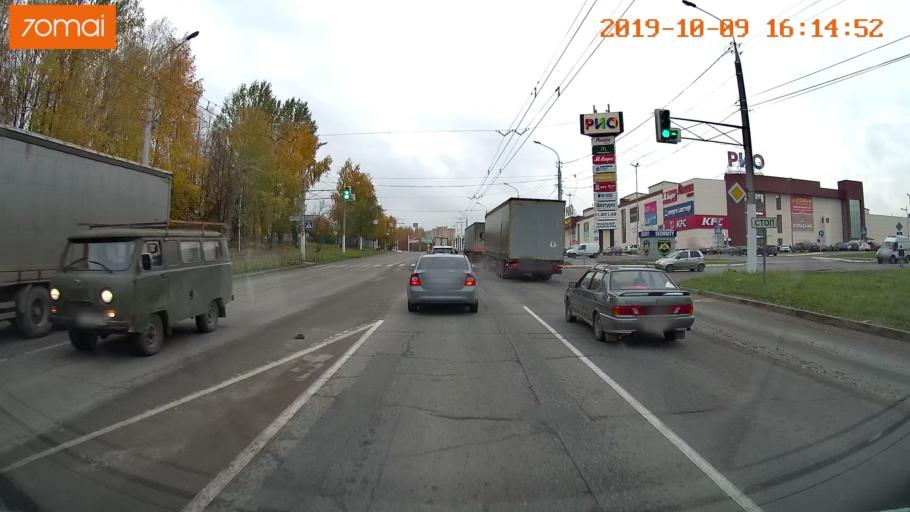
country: RU
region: Kostroma
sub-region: Kostromskoy Rayon
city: Kostroma
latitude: 57.7427
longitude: 40.9215
